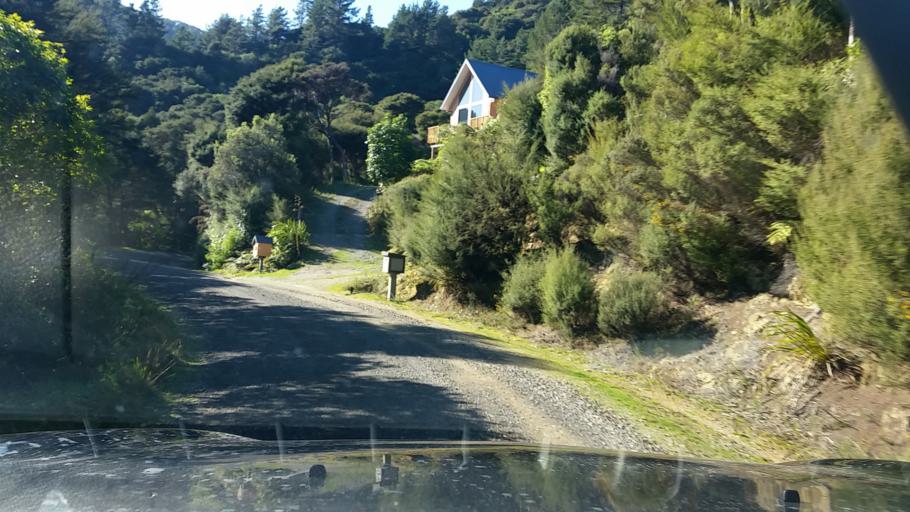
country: NZ
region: Marlborough
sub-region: Marlborough District
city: Picton
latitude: -41.1796
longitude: 173.9727
